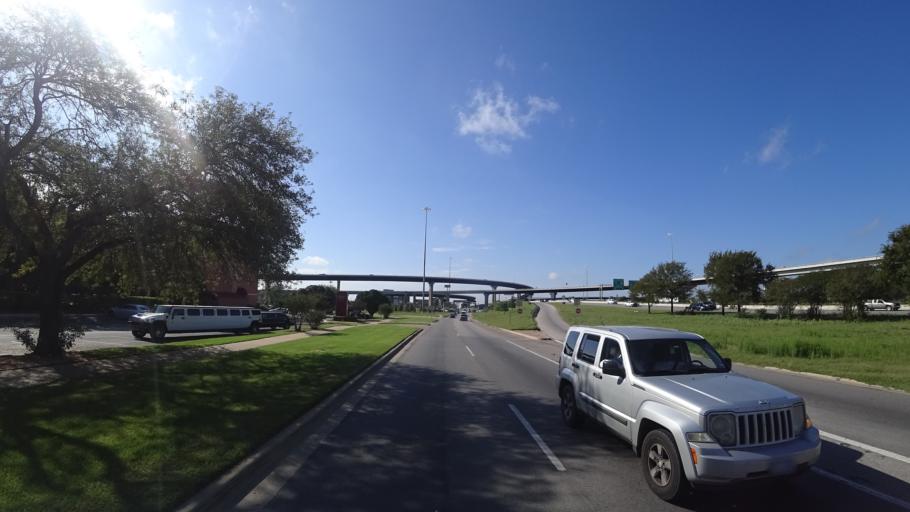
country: US
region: Texas
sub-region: Travis County
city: Austin
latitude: 30.3247
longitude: -97.7057
